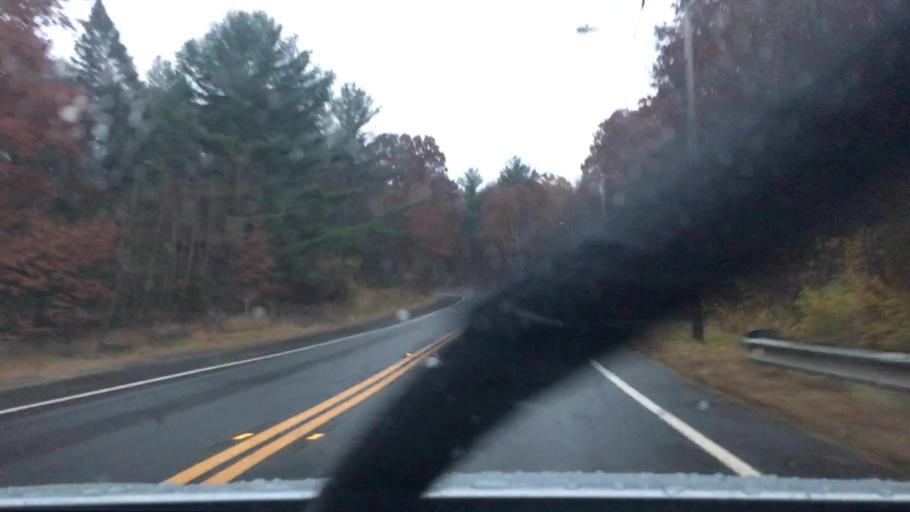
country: US
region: Massachusetts
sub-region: Hampden County
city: Southwick
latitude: 42.0624
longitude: -72.7097
